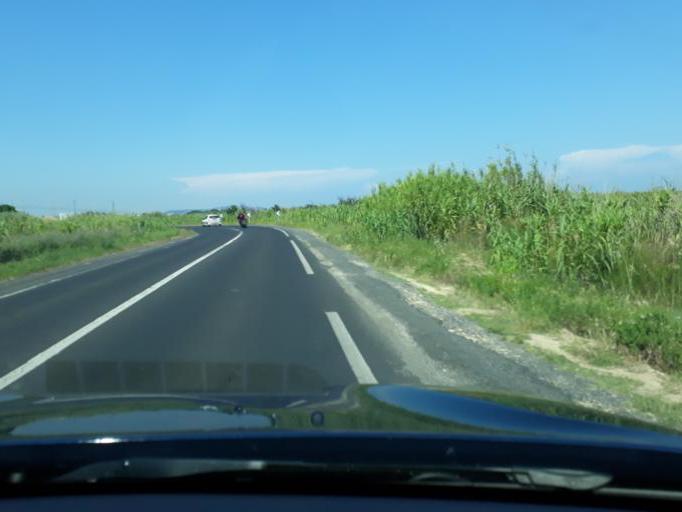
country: FR
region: Languedoc-Roussillon
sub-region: Departement de l'Herault
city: Marseillan
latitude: 43.3292
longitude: 3.5597
